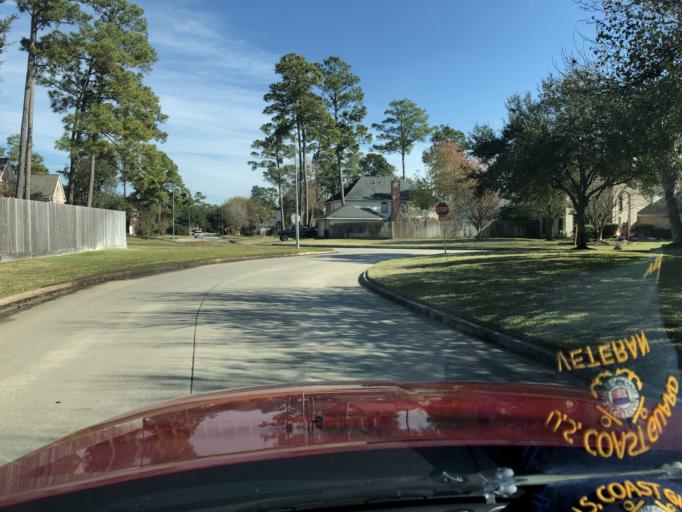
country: US
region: Texas
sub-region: Harris County
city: Tomball
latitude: 30.0216
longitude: -95.5566
